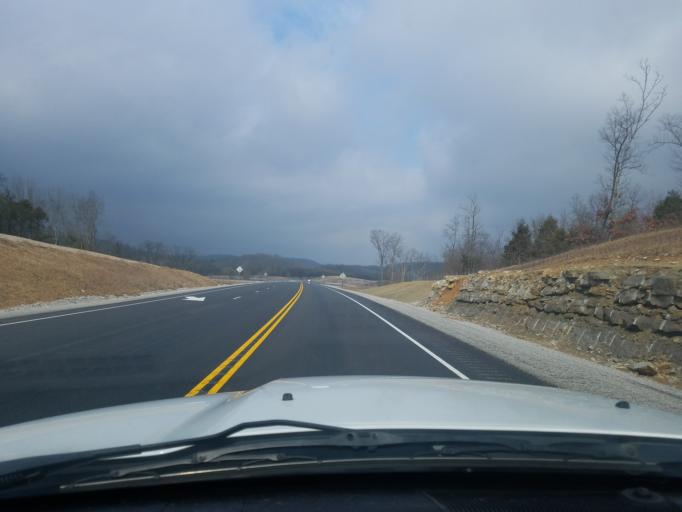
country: US
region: Kentucky
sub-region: Logan County
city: Russellville
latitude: 36.8187
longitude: -86.8662
